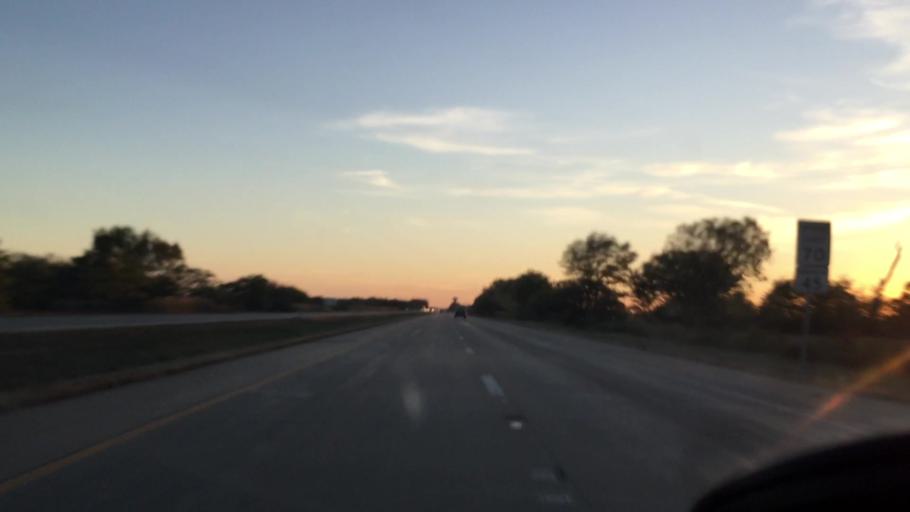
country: US
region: Illinois
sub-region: Grundy County
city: Morris
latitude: 41.4111
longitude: -88.3827
